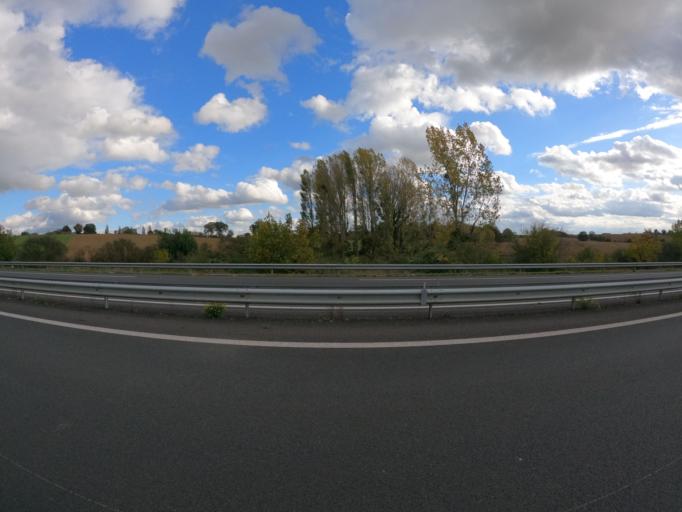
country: FR
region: Pays de la Loire
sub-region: Departement de la Sarthe
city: Etival-les-le-Mans
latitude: 47.9691
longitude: 0.0382
